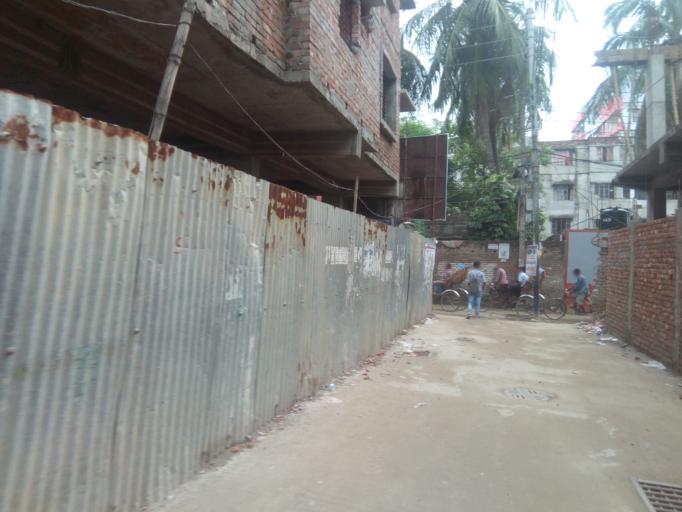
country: BD
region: Dhaka
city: Paltan
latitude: 23.7613
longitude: 90.4226
